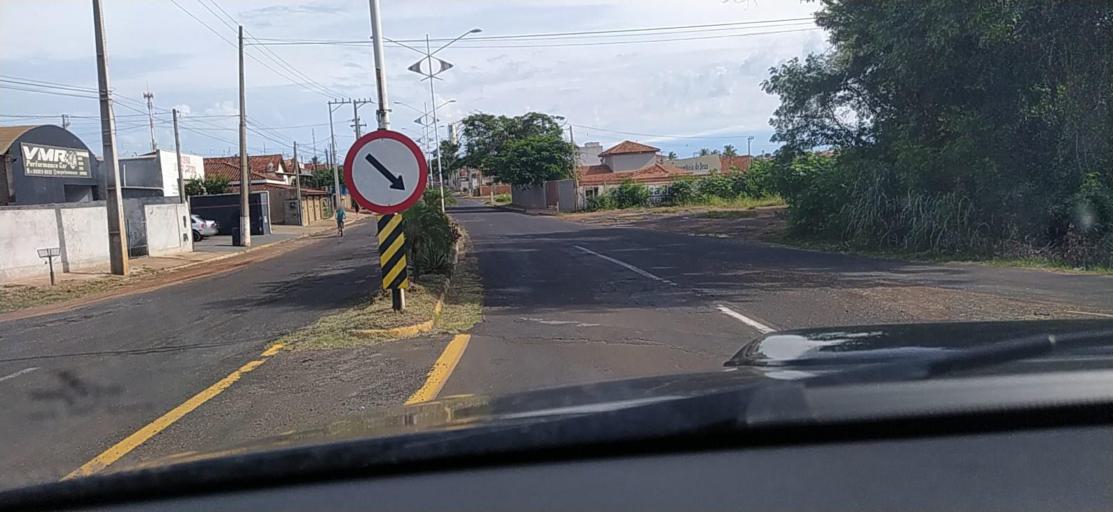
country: BR
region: Sao Paulo
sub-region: Catanduva
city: Catanduva
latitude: -21.0637
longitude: -49.0627
